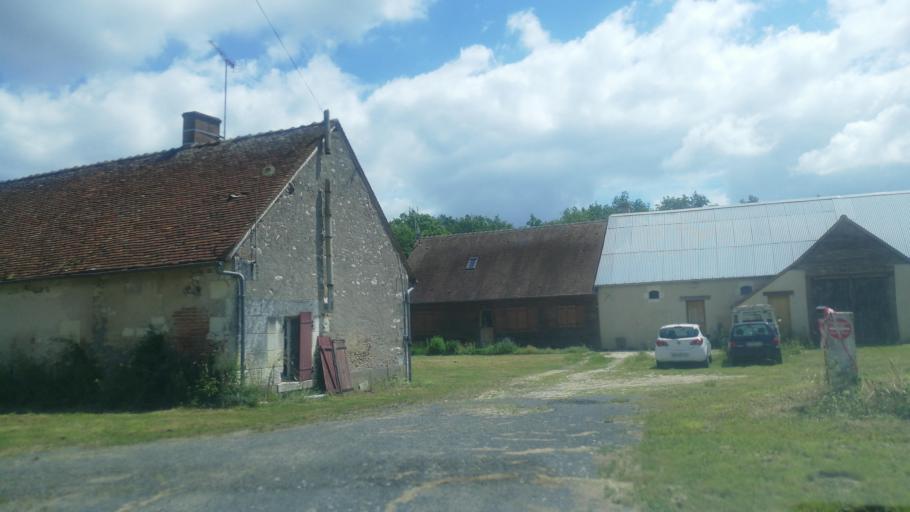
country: FR
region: Centre
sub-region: Departement du Loir-et-Cher
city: Contres
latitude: 47.3676
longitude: 1.4175
